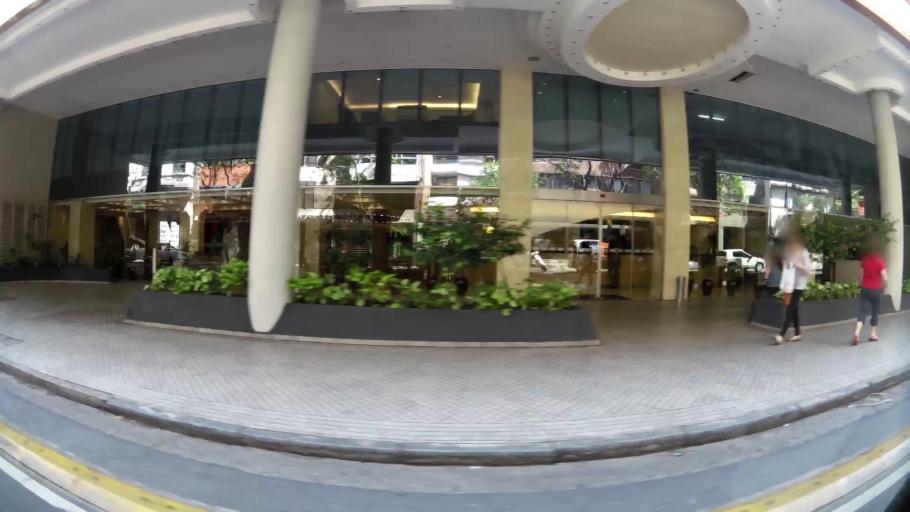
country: AR
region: Santa Fe
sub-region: Departamento de Rosario
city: Rosario
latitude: -32.9373
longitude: -60.6483
